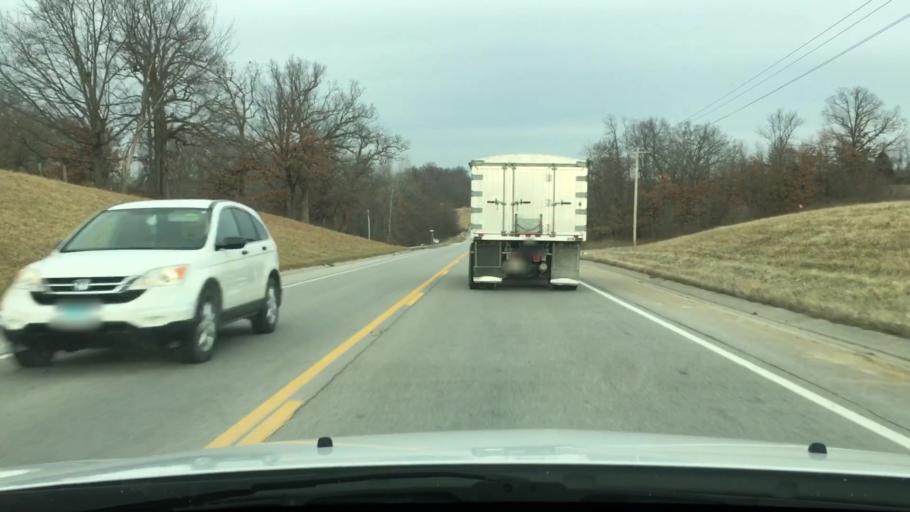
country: US
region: Illinois
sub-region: Pike County
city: Pittsfield
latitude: 39.6624
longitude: -90.7734
